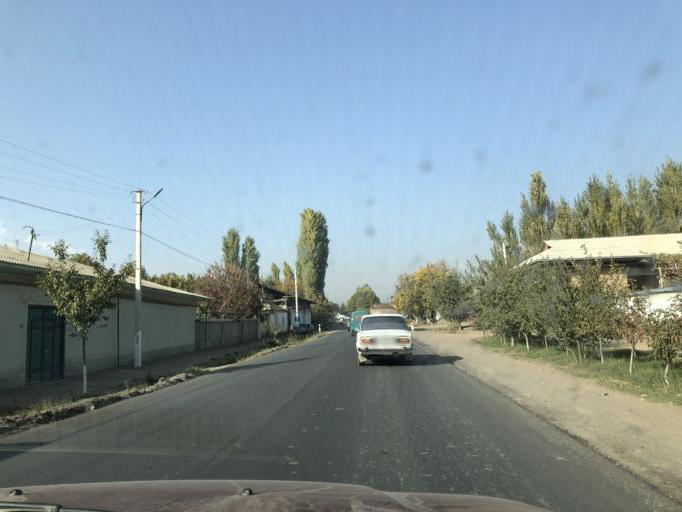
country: UZ
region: Namangan
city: Chust Shahri
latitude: 41.0699
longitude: 71.2046
